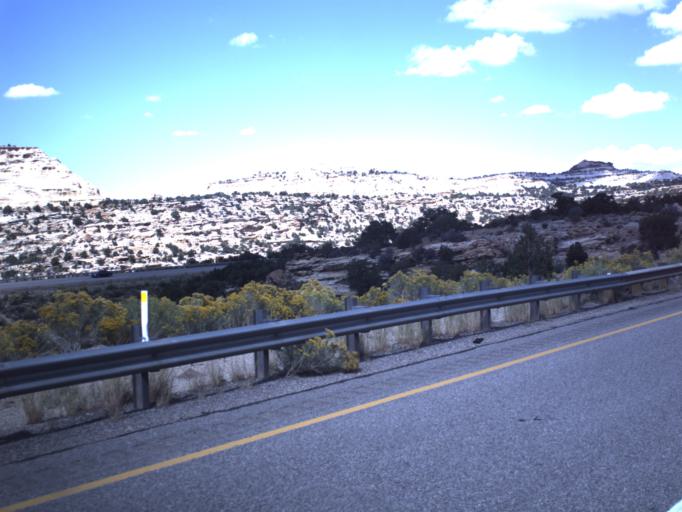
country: US
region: Utah
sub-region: Emery County
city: Ferron
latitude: 38.8574
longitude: -110.8682
